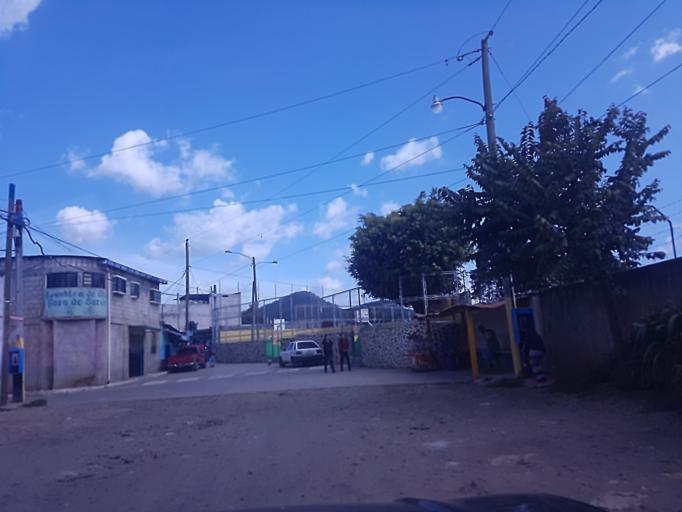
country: GT
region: Guatemala
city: Petapa
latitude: 14.5028
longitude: -90.5564
